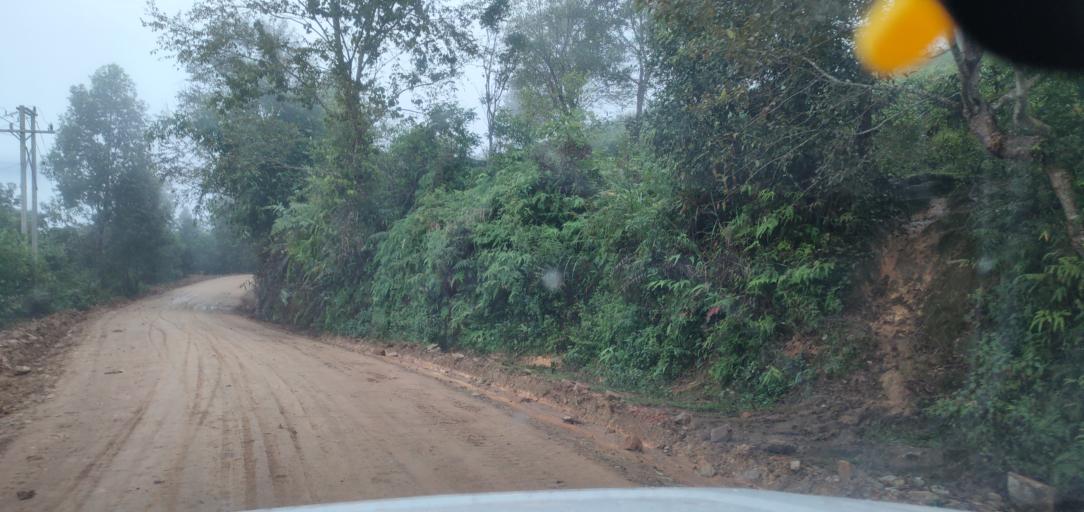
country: LA
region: Phongsali
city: Phongsali
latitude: 21.4295
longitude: 102.2608
